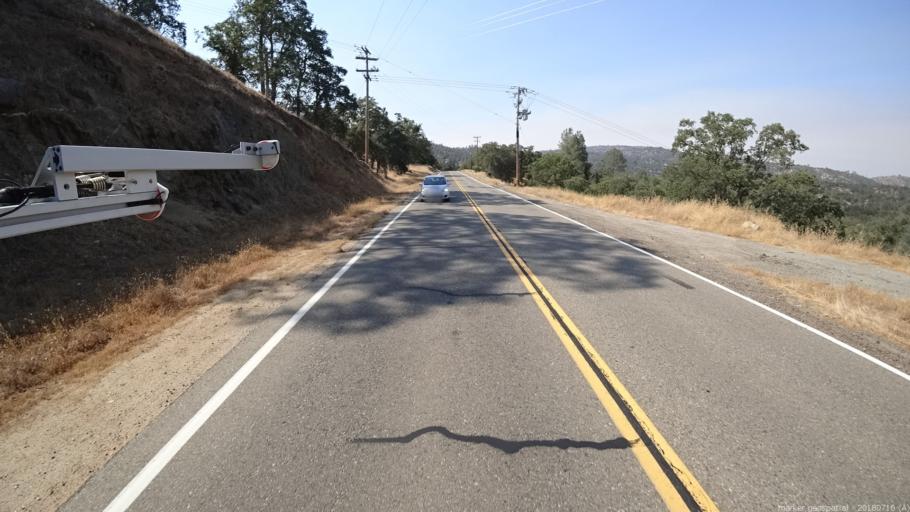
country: US
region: California
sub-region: Madera County
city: Yosemite Lakes
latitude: 37.2238
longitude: -119.7688
